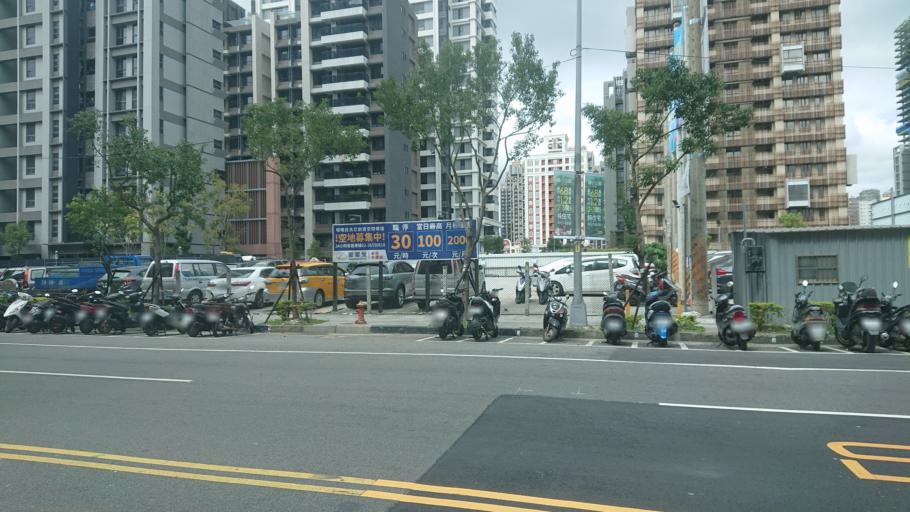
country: TW
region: Taipei
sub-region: Taipei
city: Banqiao
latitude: 25.0545
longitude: 121.4575
